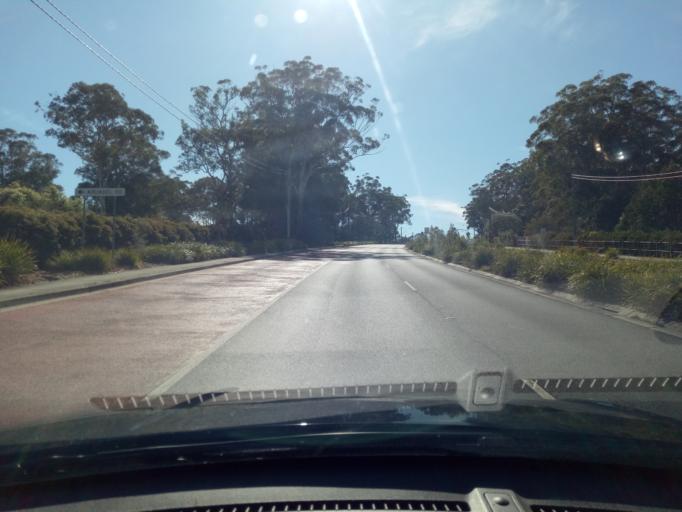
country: AU
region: New South Wales
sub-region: Gosford Shire
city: Erina
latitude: -33.4265
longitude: 151.3971
